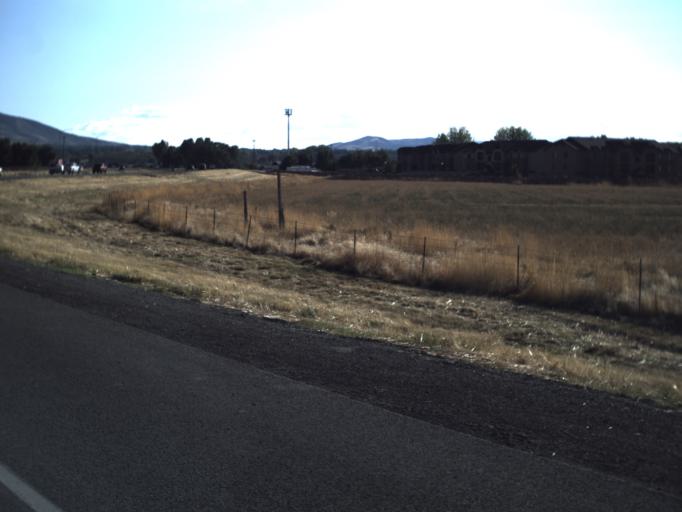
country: US
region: Utah
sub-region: Utah County
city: Payson
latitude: 40.0310
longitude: -111.7587
